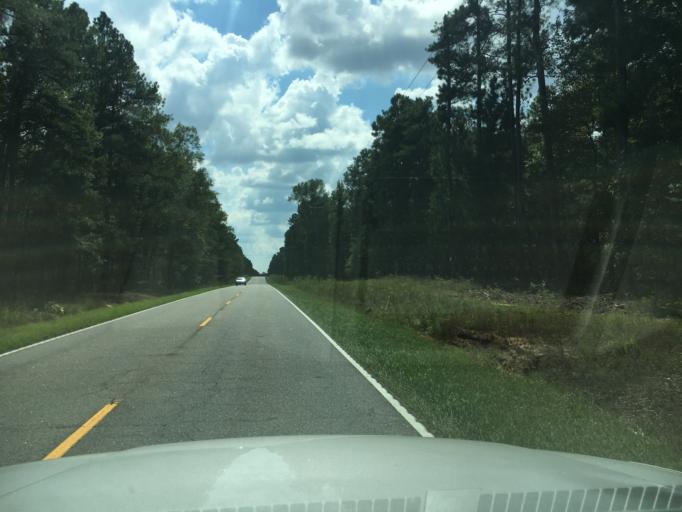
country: US
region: South Carolina
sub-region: Greenwood County
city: Greenwood
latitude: 34.0963
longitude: -82.1294
